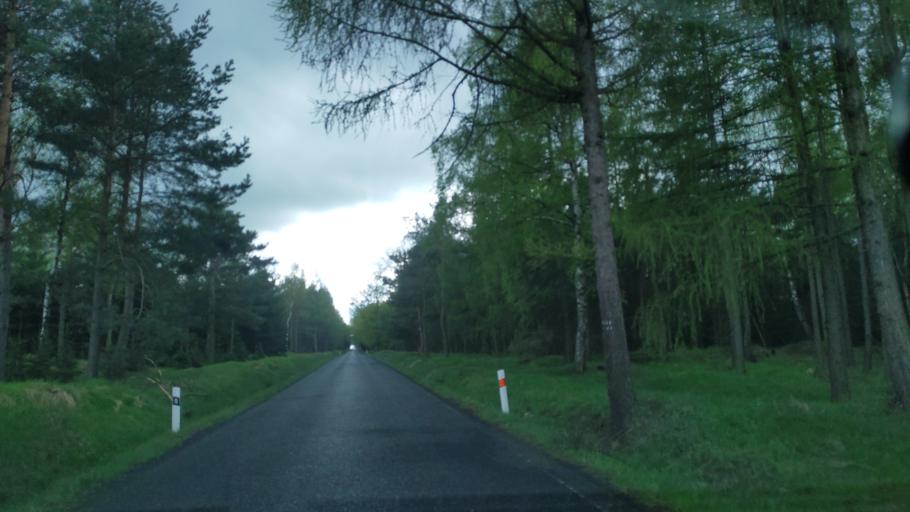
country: CZ
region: Ustecky
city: Libouchec
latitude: 50.7895
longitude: 14.0694
